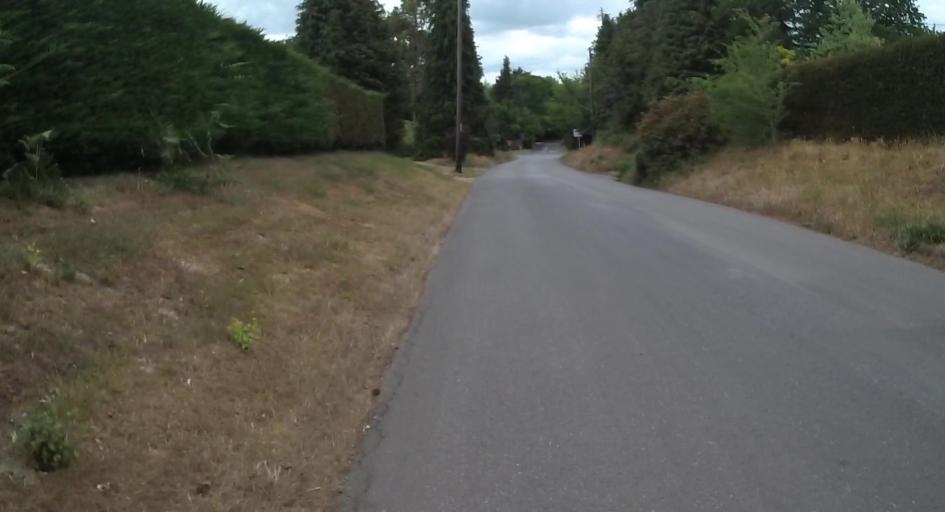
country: GB
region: England
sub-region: Surrey
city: Seale
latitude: 51.2212
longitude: -0.7333
